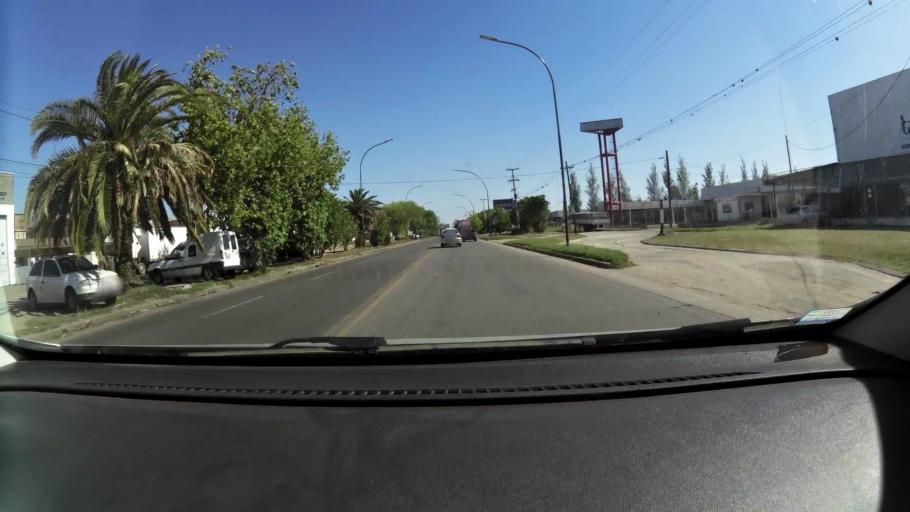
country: AR
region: Cordoba
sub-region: Departamento de Capital
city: Cordoba
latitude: -31.3658
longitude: -64.1762
